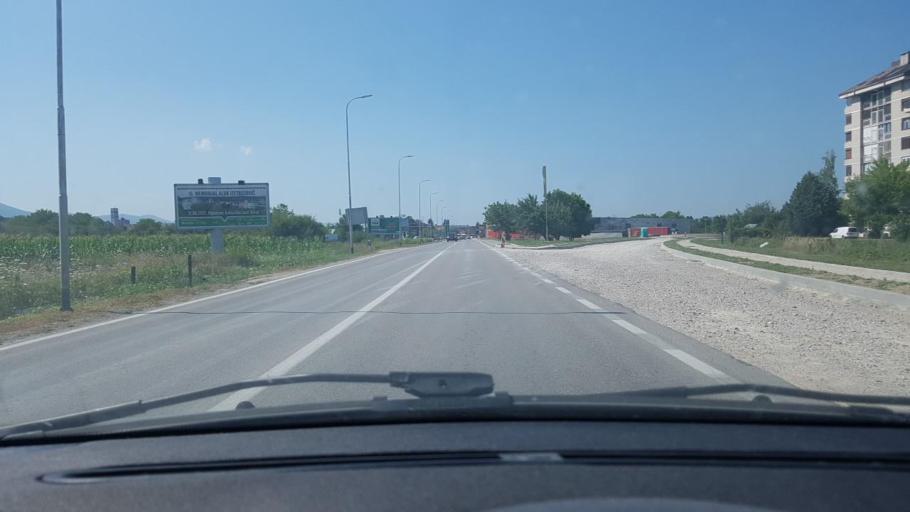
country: BA
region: Federation of Bosnia and Herzegovina
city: Bihac
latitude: 44.8104
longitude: 15.8826
